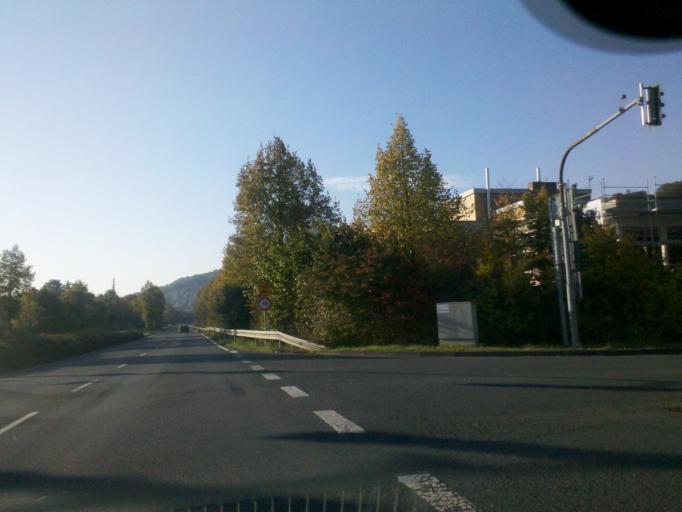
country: DE
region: Hesse
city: Dillenburg
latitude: 50.7339
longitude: 8.2910
